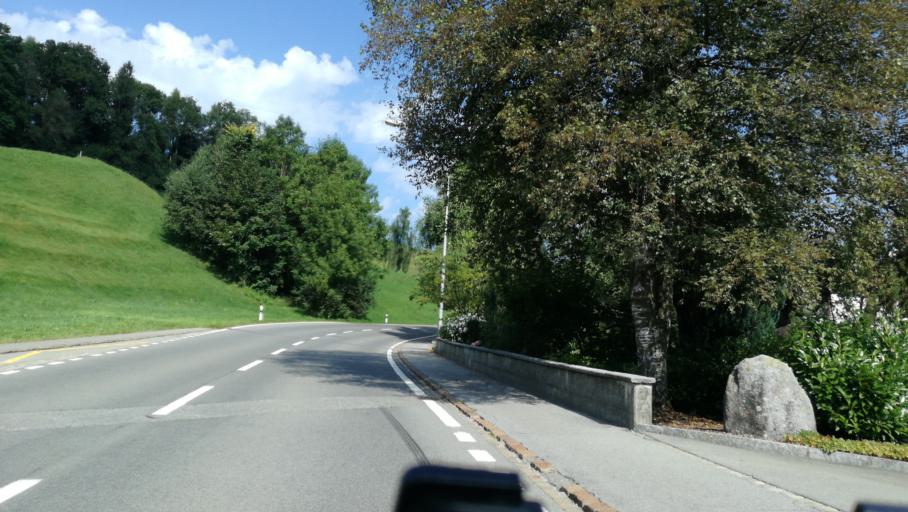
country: CH
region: Zug
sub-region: Zug
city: Unterageri
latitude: 47.1598
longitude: 8.5582
